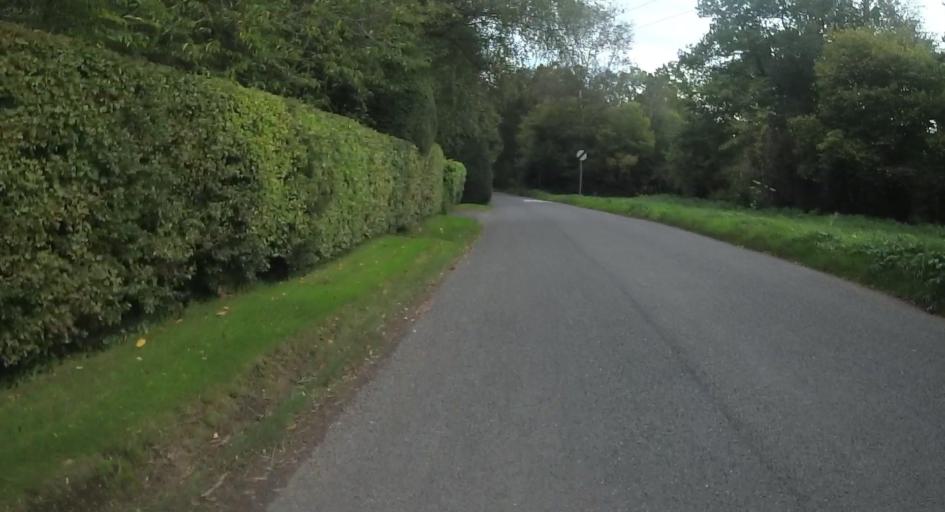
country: GB
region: England
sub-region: Hampshire
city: Hook
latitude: 51.3071
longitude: -0.9309
